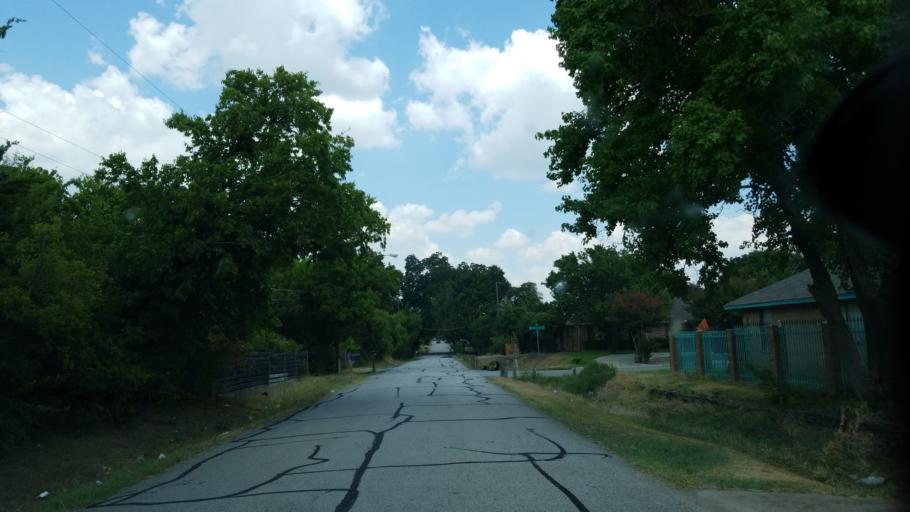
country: US
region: Texas
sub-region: Dallas County
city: Duncanville
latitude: 32.6770
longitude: -96.9040
